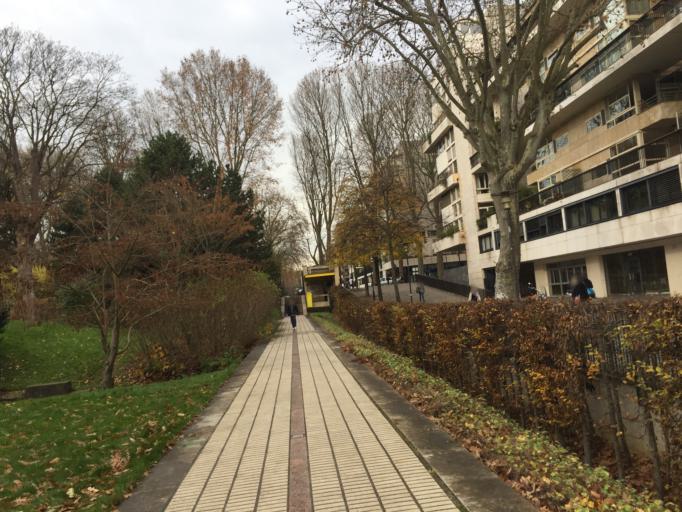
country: FR
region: Ile-de-France
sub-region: Departement du Val-de-Marne
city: Ivry-sur-Seine
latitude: 48.8343
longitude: 2.3852
